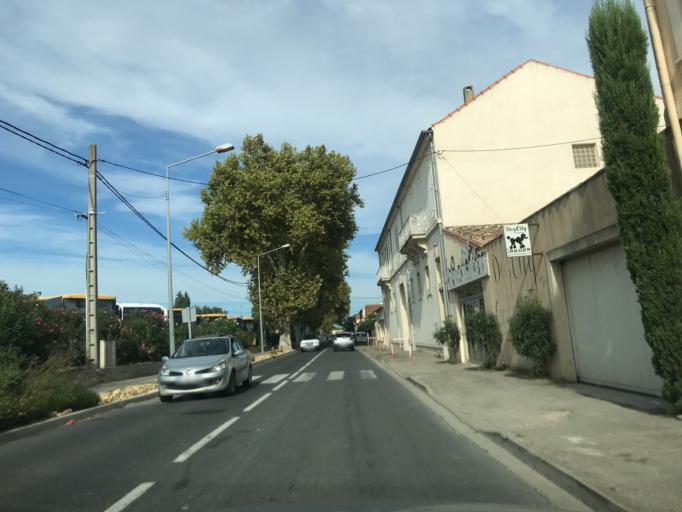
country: FR
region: Languedoc-Roussillon
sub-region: Departement du Gard
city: Aigues-Mortes
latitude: 43.5709
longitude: 4.1919
